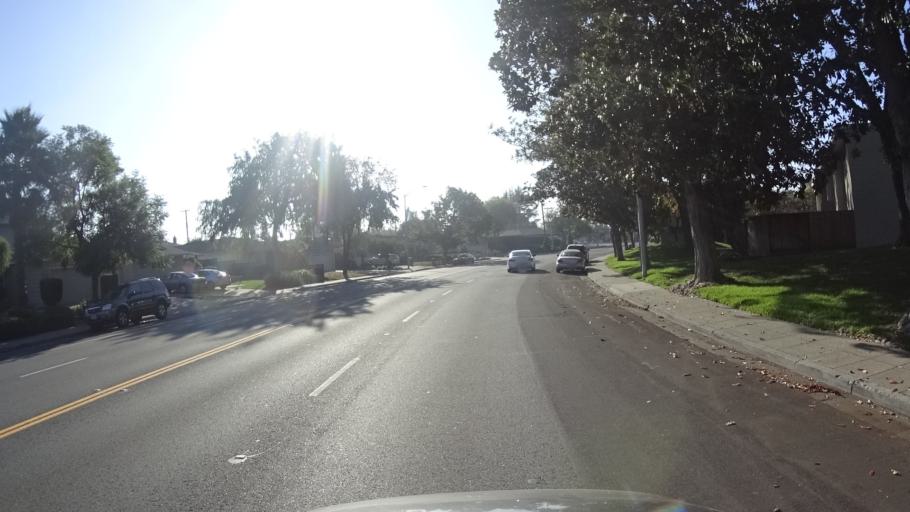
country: US
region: California
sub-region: Santa Clara County
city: Santa Clara
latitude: 37.3455
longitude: -121.9854
